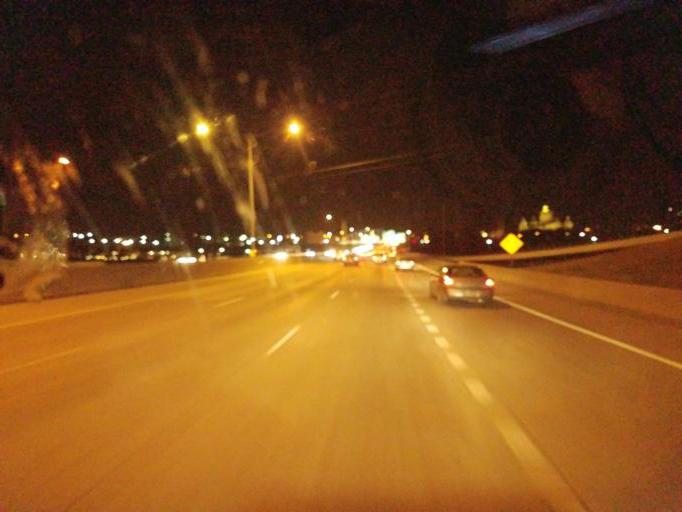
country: US
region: Iowa
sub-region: Polk County
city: Des Moines
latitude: 41.5956
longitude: -93.6193
